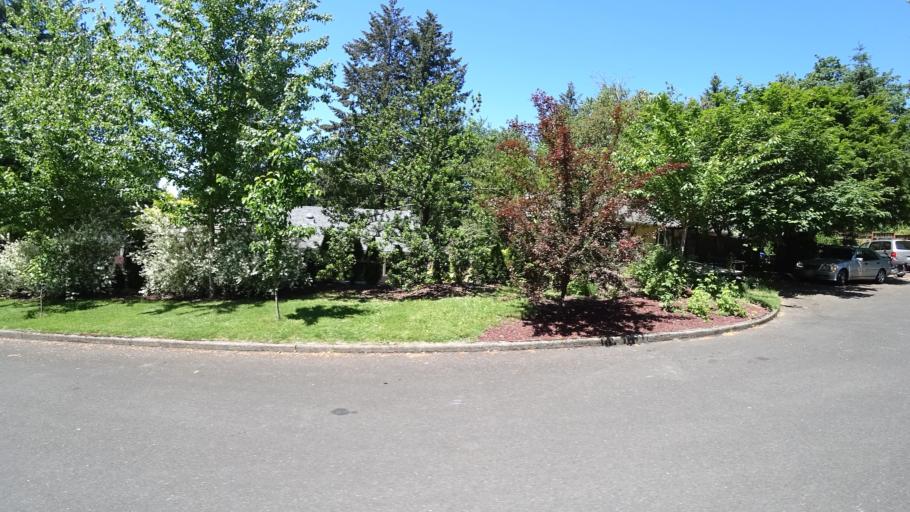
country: US
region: Oregon
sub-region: Washington County
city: Raleigh Hills
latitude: 45.4893
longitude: -122.7136
